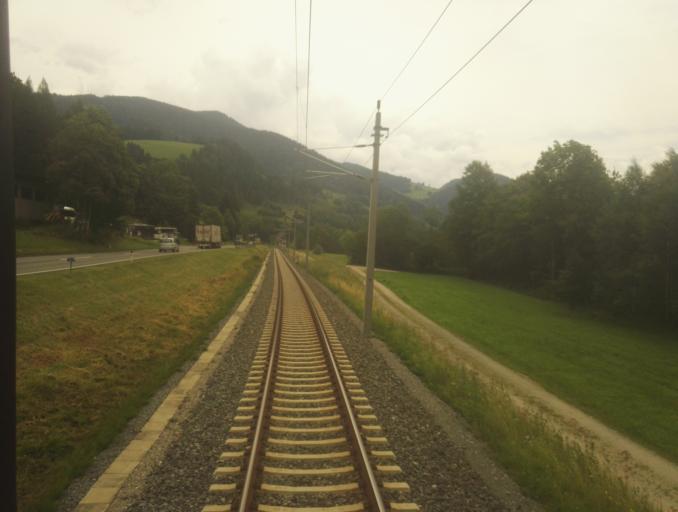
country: AT
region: Salzburg
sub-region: Politischer Bezirk Sankt Johann im Pongau
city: Forstau
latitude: 47.4020
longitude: 13.5544
